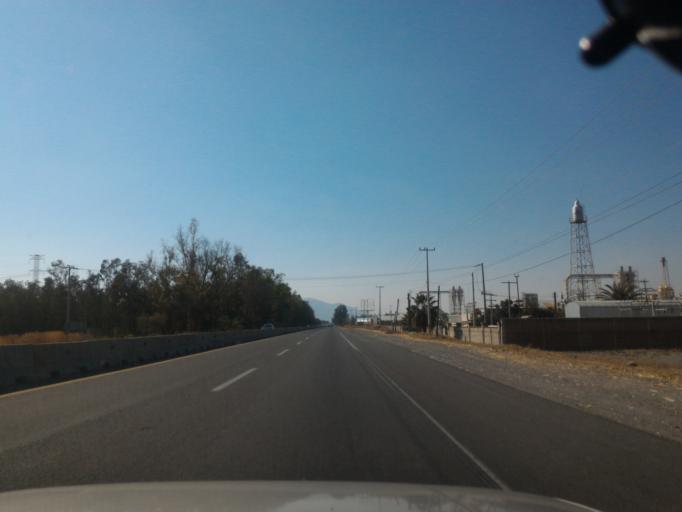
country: MX
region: Jalisco
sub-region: Poncitlan
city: Santa Cruz el Grande
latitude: 20.3655
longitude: -102.8432
